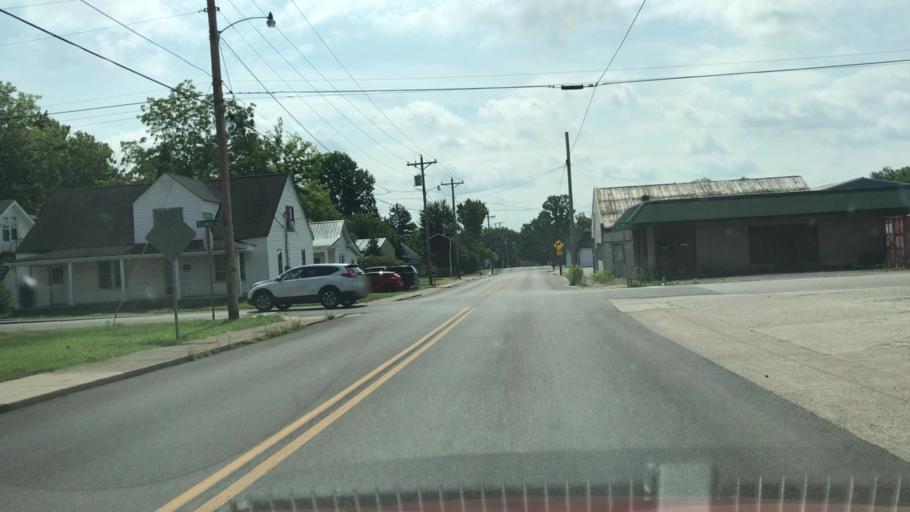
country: US
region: Kentucky
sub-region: Barren County
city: Glasgow
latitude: 36.9926
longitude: -85.9117
